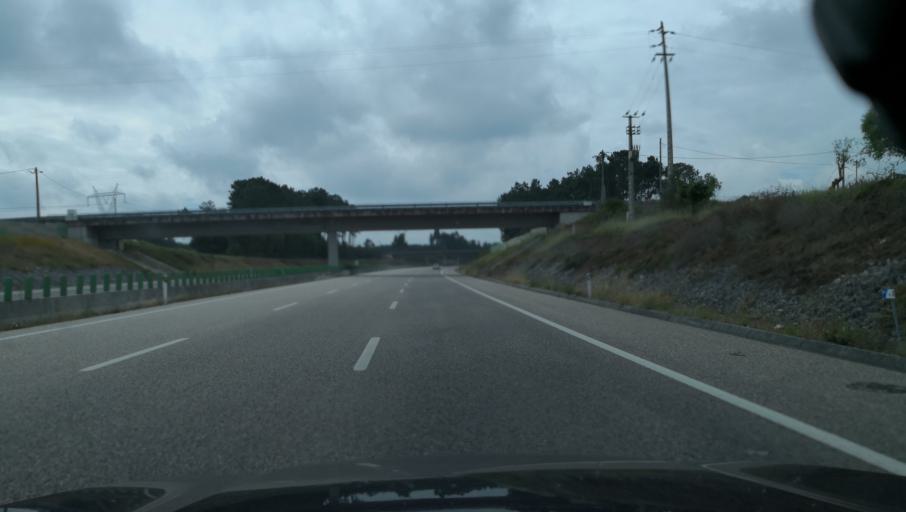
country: PT
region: Leiria
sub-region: Pombal
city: Lourical
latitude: 39.9676
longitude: -8.7794
